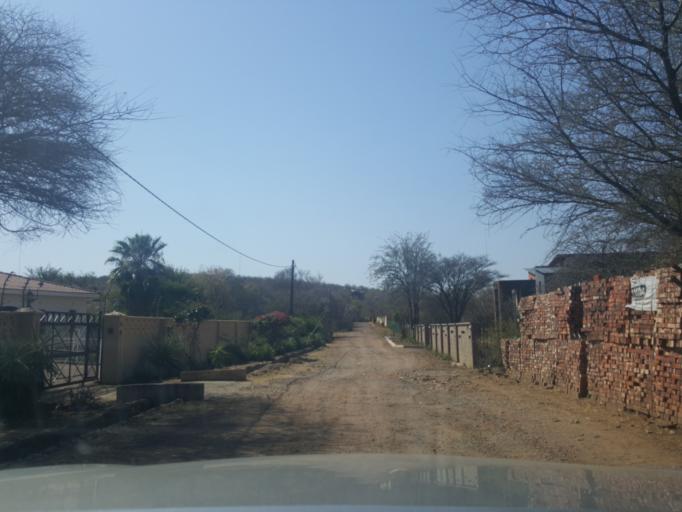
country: BW
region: Kweneng
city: Gabane
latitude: -24.7433
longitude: 25.8295
